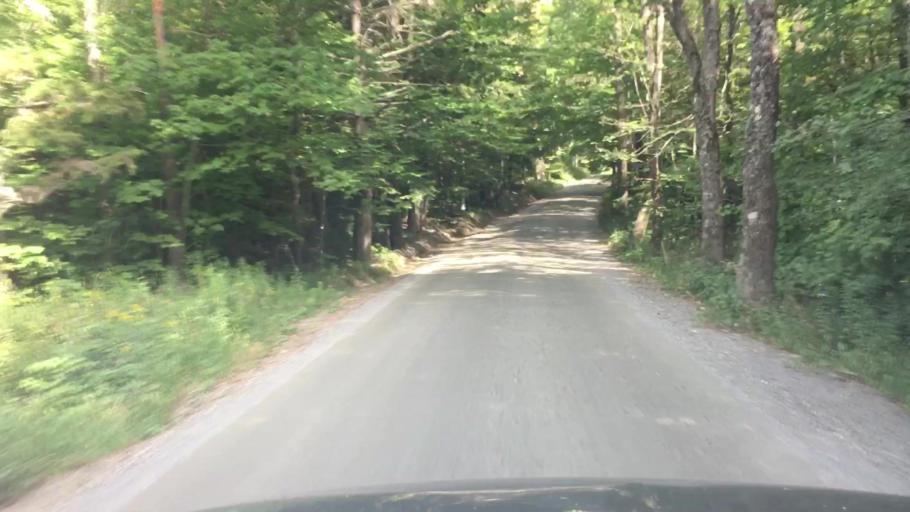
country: US
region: Vermont
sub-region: Windham County
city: Dover
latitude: 42.8219
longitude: -72.7667
